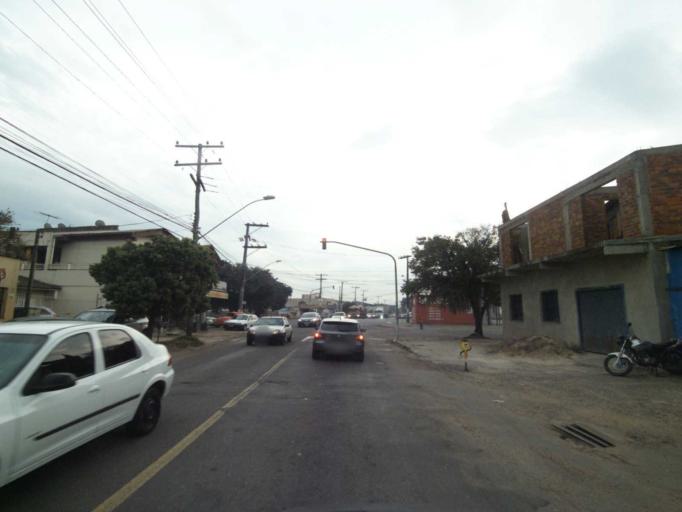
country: BR
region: Rio Grande do Sul
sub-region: Sao Leopoldo
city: Sao Leopoldo
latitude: -29.7732
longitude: -51.1559
